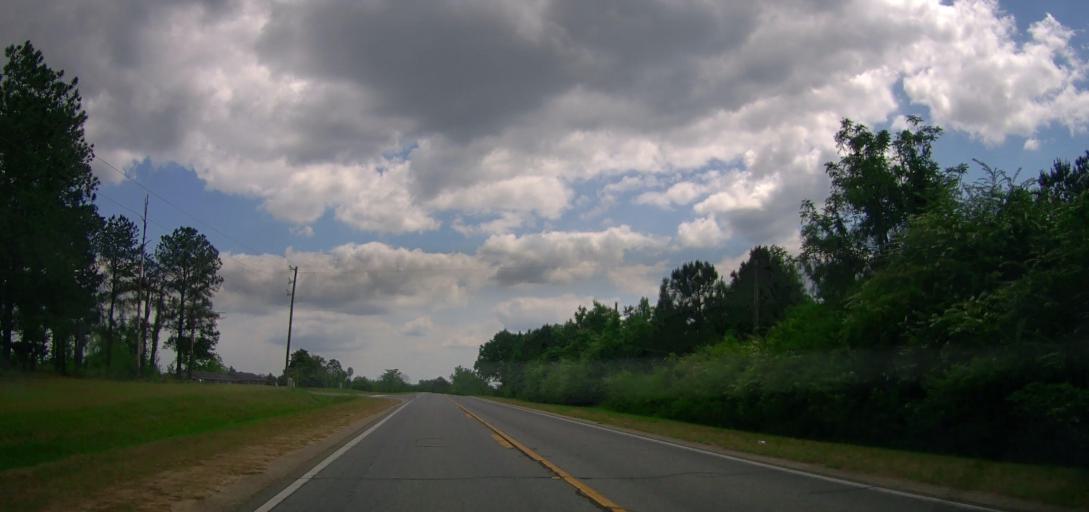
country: US
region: Georgia
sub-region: Laurens County
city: East Dublin
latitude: 32.5073
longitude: -82.8368
